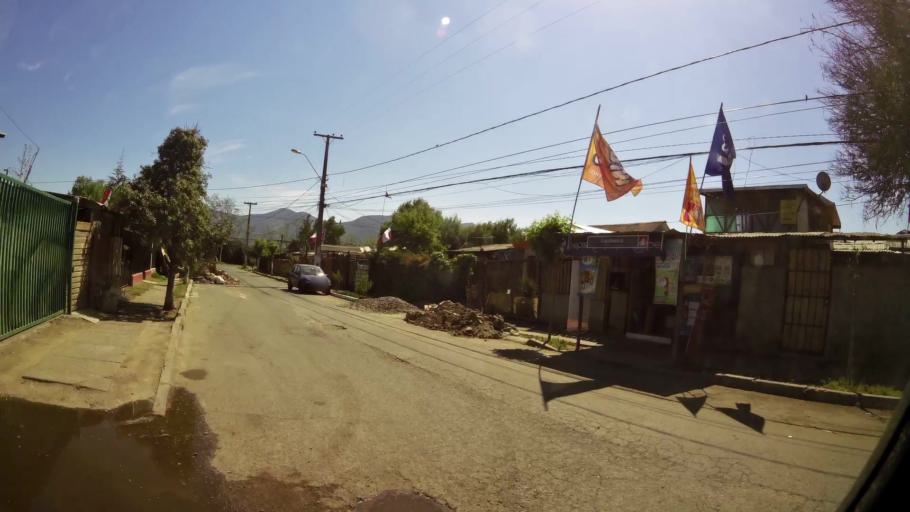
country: CL
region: Santiago Metropolitan
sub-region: Provincia de Talagante
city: Penaflor
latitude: -33.6129
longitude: -70.9049
